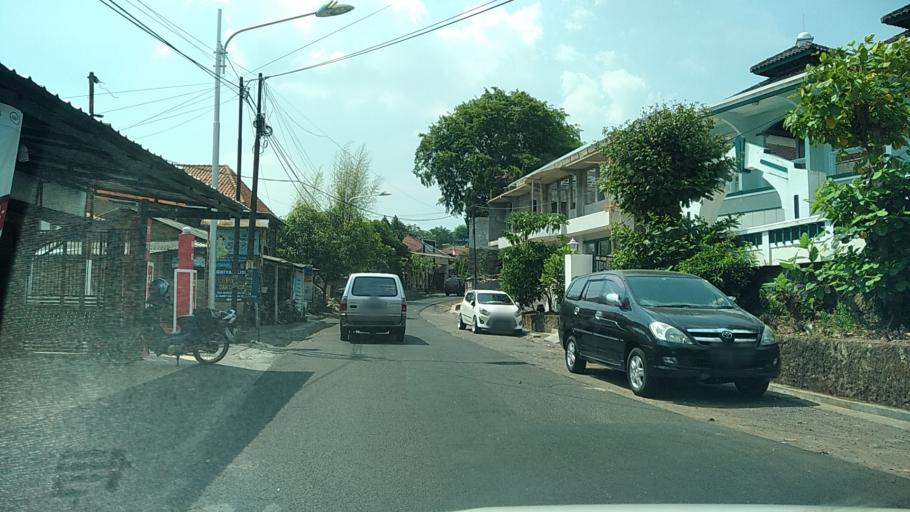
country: ID
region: Central Java
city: Semarang
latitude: -7.0093
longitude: 110.4124
